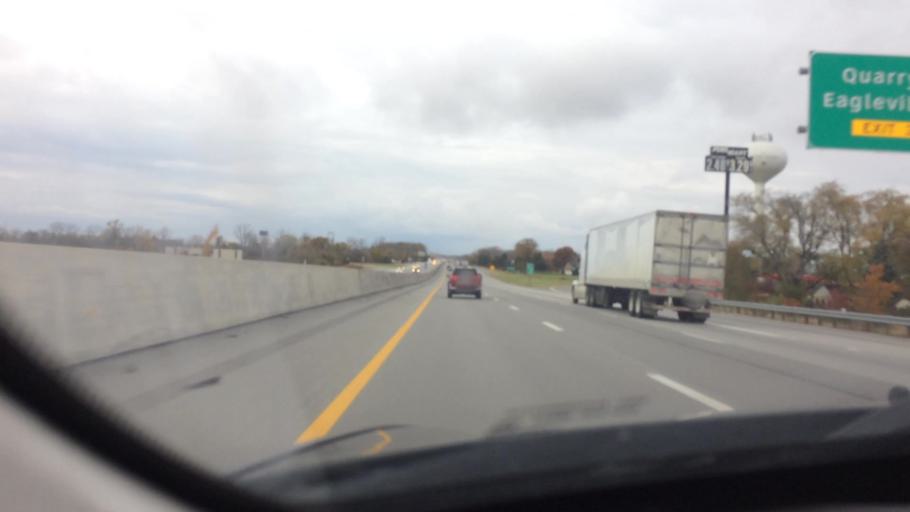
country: US
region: Ohio
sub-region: Wood County
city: North Baltimore
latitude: 41.1832
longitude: -83.6495
